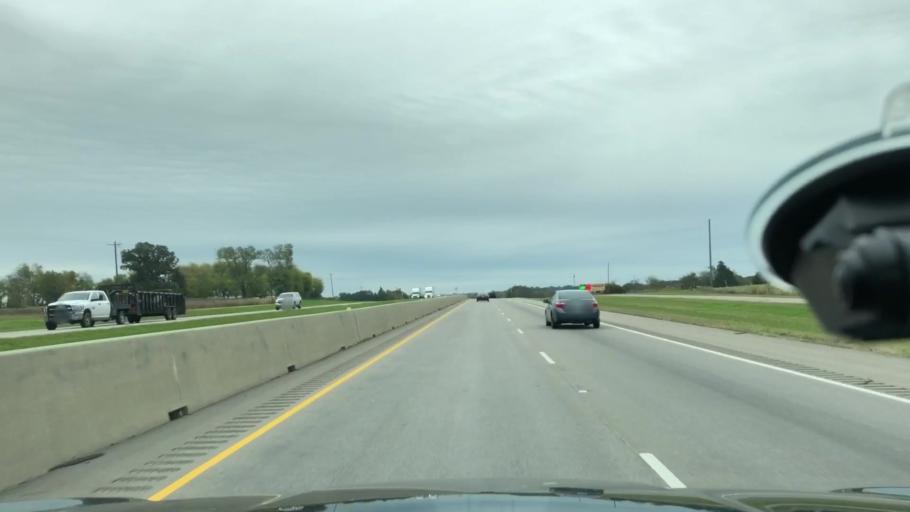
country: US
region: Texas
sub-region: Franklin County
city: Mount Vernon
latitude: 33.1638
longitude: -95.2689
